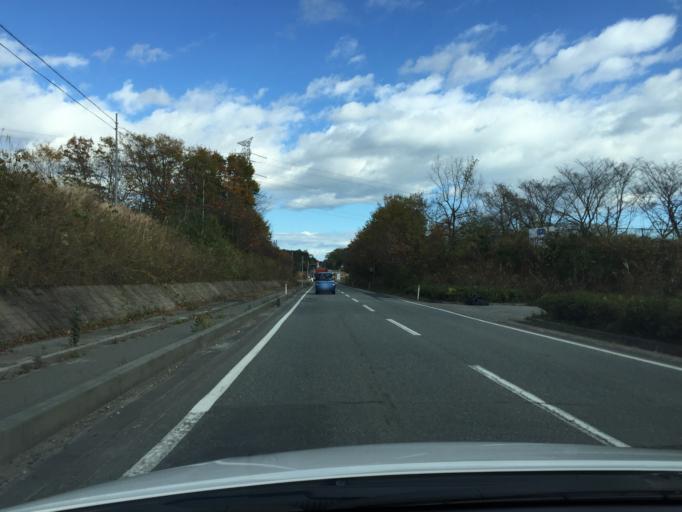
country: JP
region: Fukushima
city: Namie
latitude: 37.4236
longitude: 141.0042
